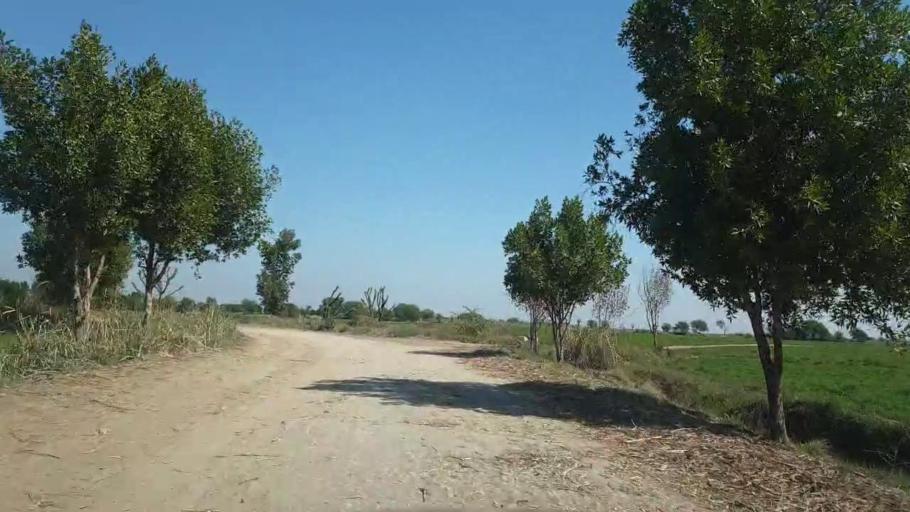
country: PK
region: Sindh
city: Mirpur Khas
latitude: 25.5964
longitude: 69.1133
